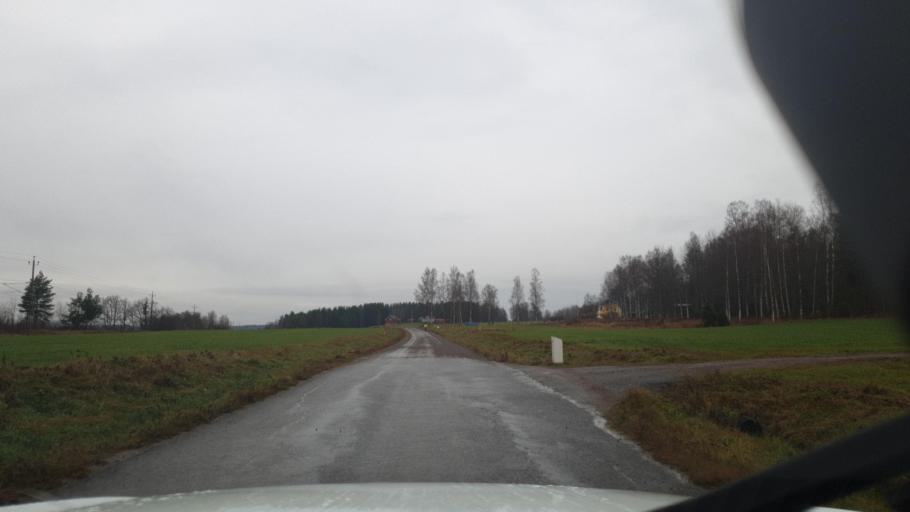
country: SE
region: Vaermland
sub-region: Eda Kommun
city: Amotfors
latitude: 59.8032
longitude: 12.3643
